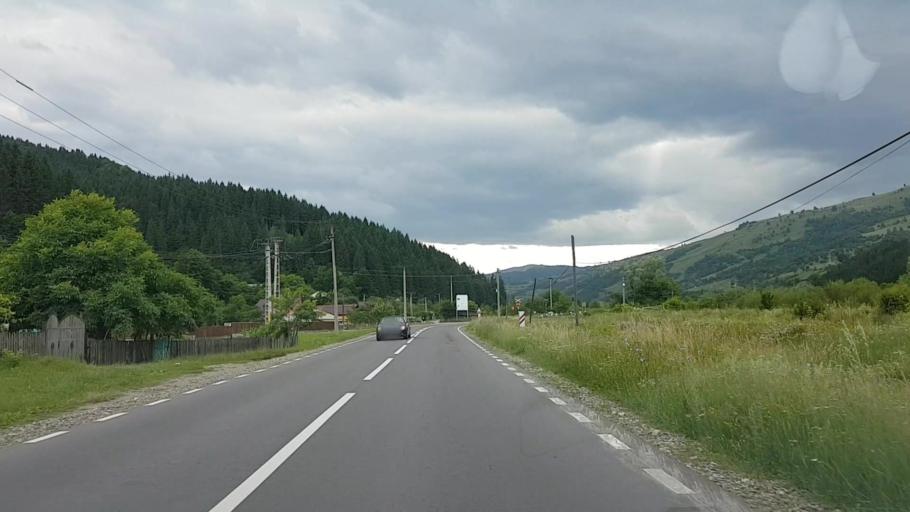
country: RO
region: Neamt
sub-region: Comuna Tasca
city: Tasca
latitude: 46.8795
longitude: 25.9873
